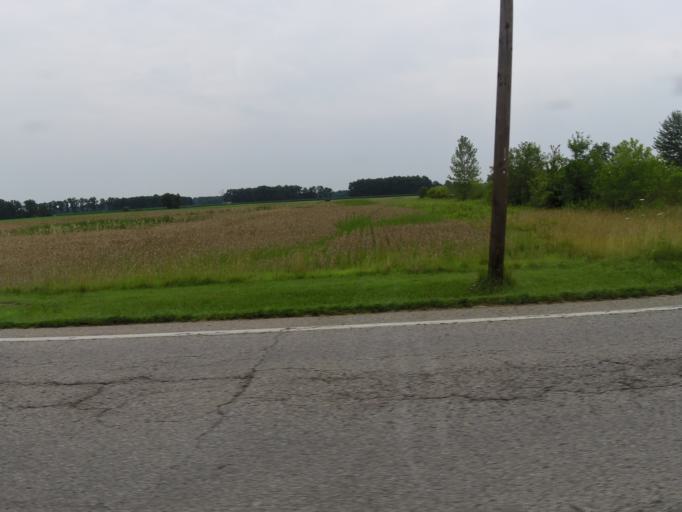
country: US
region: Ohio
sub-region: Brown County
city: Mount Orab
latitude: 39.0827
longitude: -83.9278
